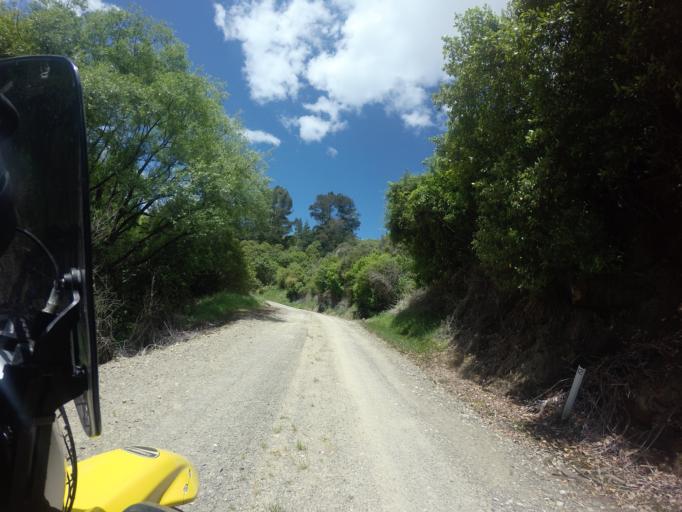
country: NZ
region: Hawke's Bay
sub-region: Wairoa District
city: Wairoa
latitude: -38.9740
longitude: 177.6784
